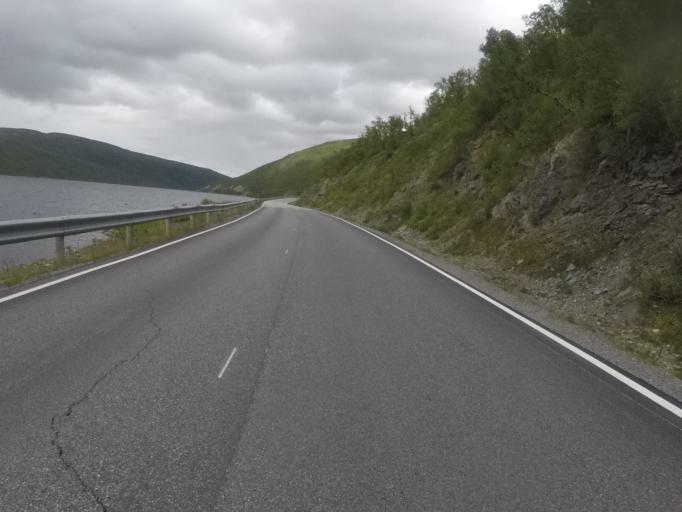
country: NO
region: Finnmark Fylke
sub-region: Alta
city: Alta
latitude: 69.6862
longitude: 23.4276
